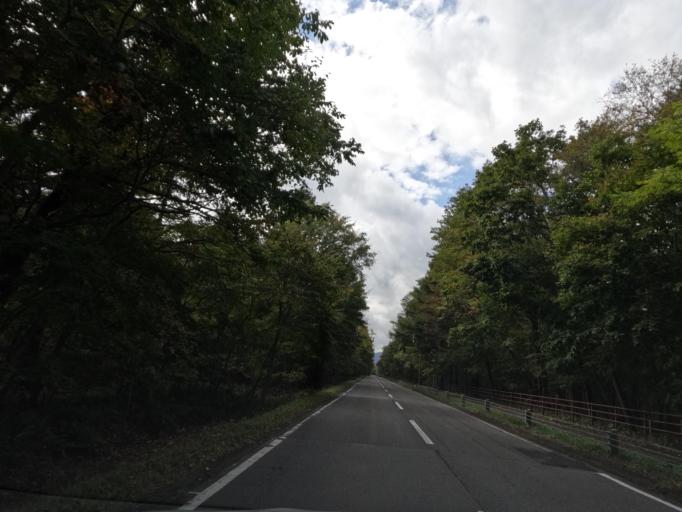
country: JP
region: Hokkaido
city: Chitose
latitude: 42.7917
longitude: 141.5357
